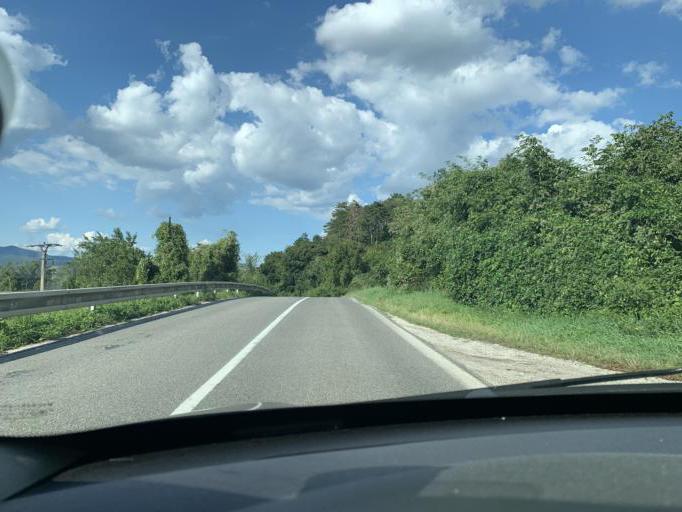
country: SK
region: Trenciansky
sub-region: Okres Nove Mesto nad Vahom
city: Nove Mesto nad Vahom
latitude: 48.8056
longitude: 17.9112
